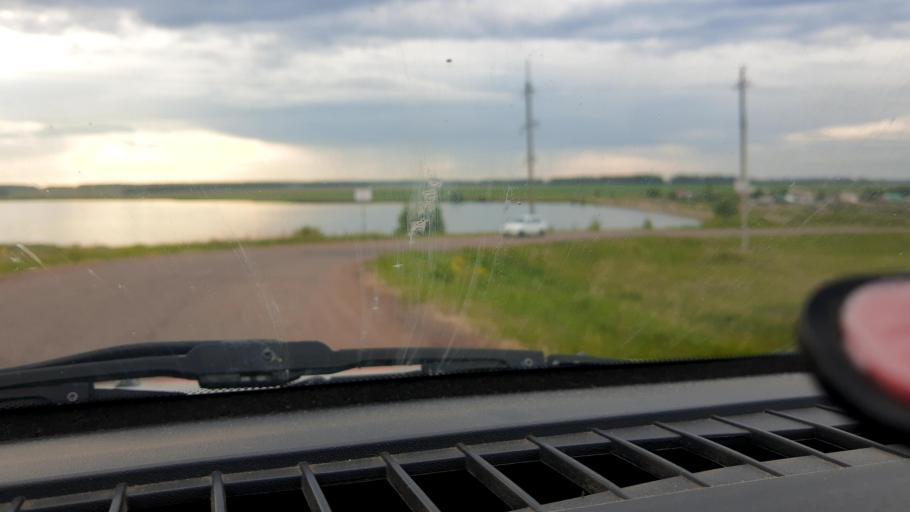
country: RU
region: Bashkortostan
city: Asanovo
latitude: 54.8485
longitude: 55.5941
